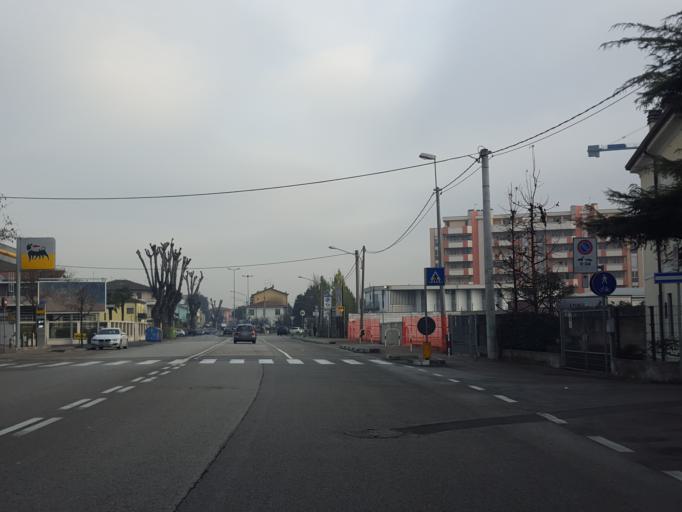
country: IT
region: Veneto
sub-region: Provincia di Vicenza
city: Vicenza
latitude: 45.5485
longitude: 11.5187
